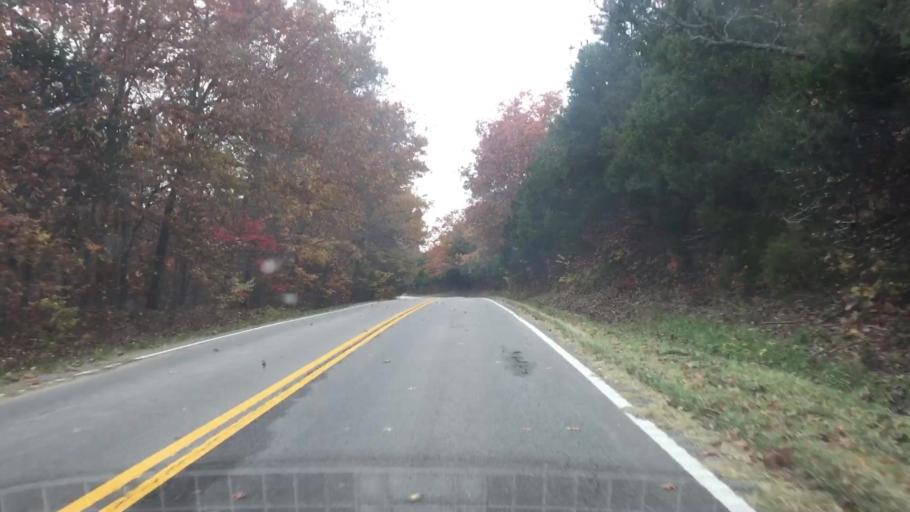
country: US
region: Missouri
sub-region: Gasconade County
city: Hermann
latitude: 38.7087
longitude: -91.6273
